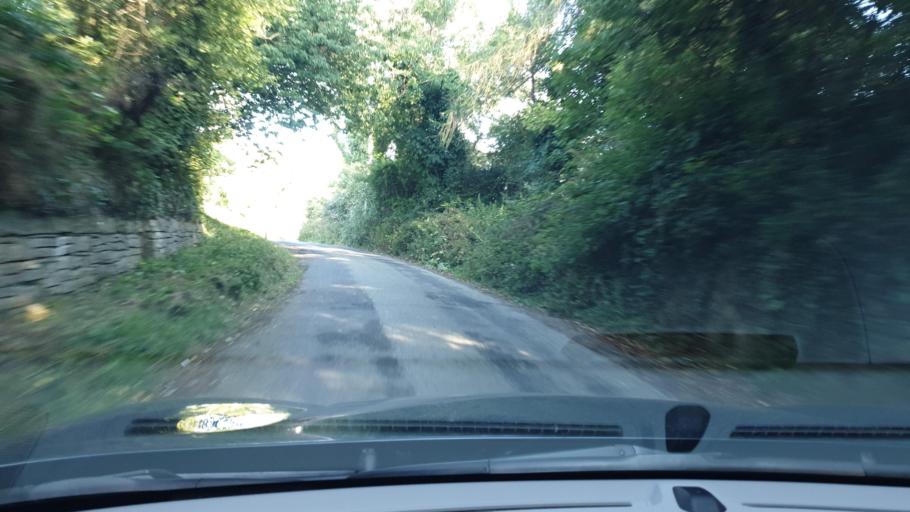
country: IE
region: Leinster
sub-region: An Mhi
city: Stamullin
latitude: 53.6008
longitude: -6.2702
